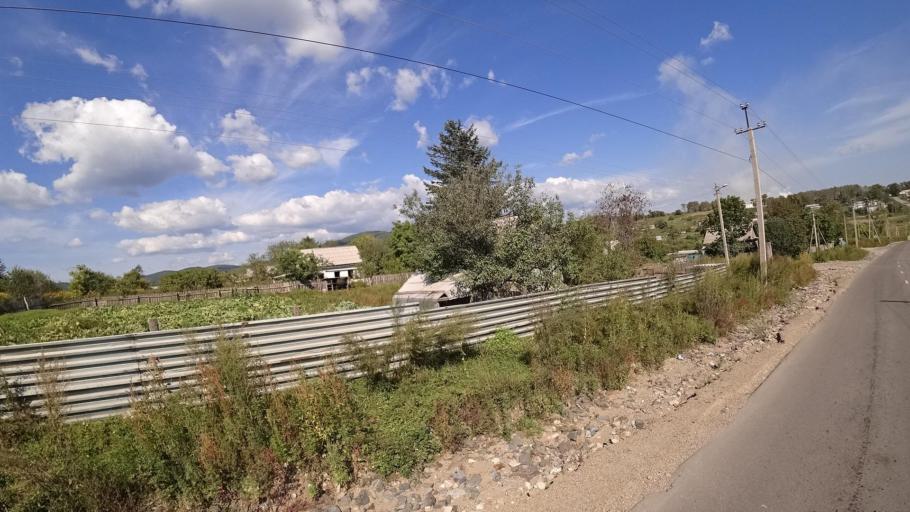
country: RU
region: Jewish Autonomous Oblast
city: Londoko
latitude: 49.0069
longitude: 131.8711
